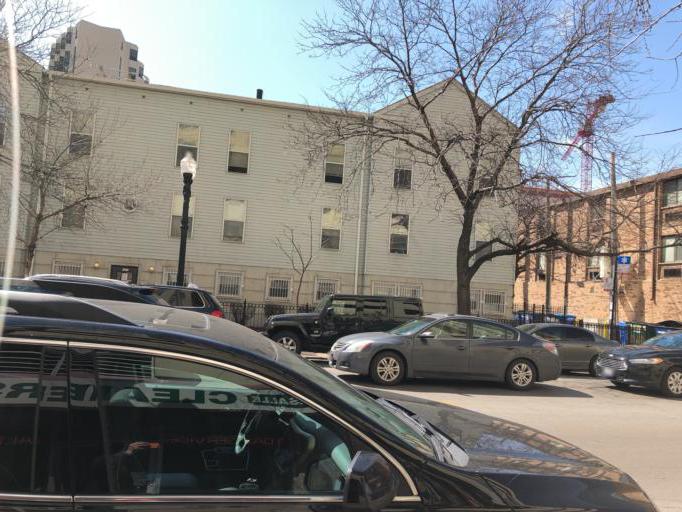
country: US
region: Illinois
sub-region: Cook County
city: Chicago
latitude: 41.9039
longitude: -87.6336
